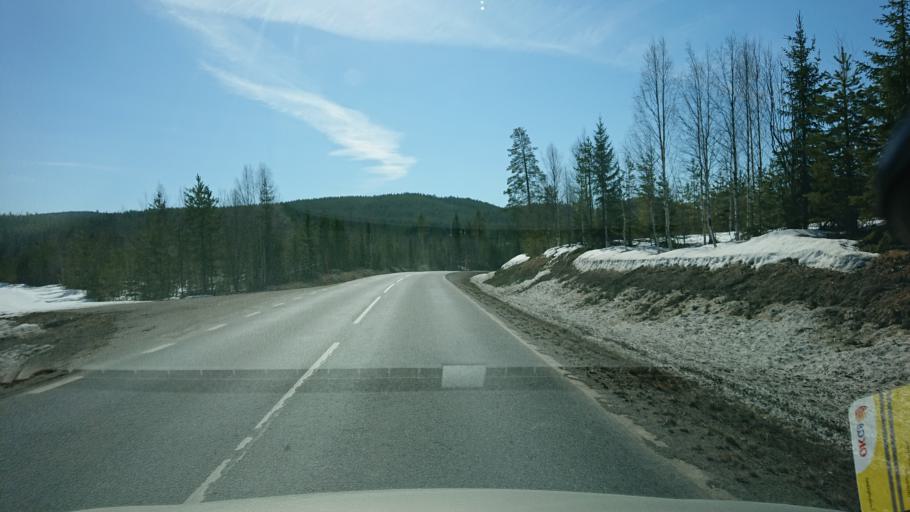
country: SE
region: Vaesterbotten
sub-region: Dorotea Kommun
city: Dorotea
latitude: 64.0609
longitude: 16.2619
